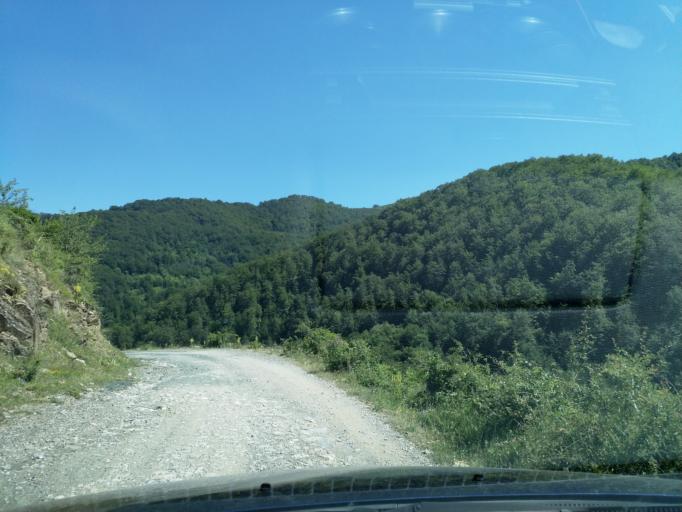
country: XK
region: Mitrovica
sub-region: Komuna e Leposaviqit
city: Leposaviq
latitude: 43.2649
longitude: 20.8620
